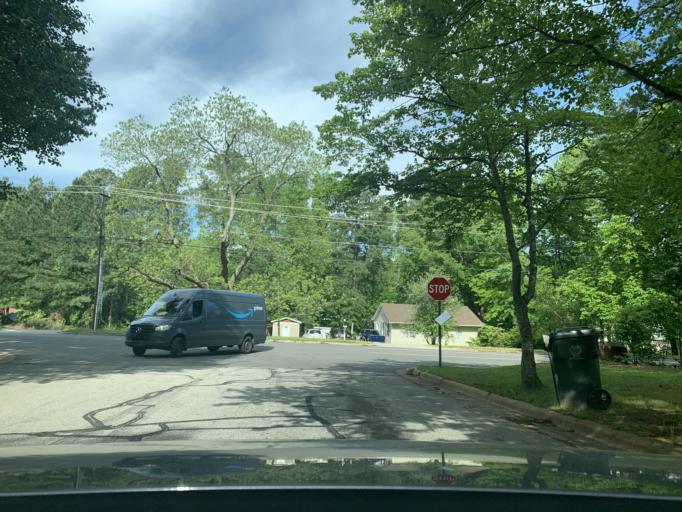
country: US
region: North Carolina
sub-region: Wake County
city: Garner
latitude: 35.7430
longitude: -78.6068
